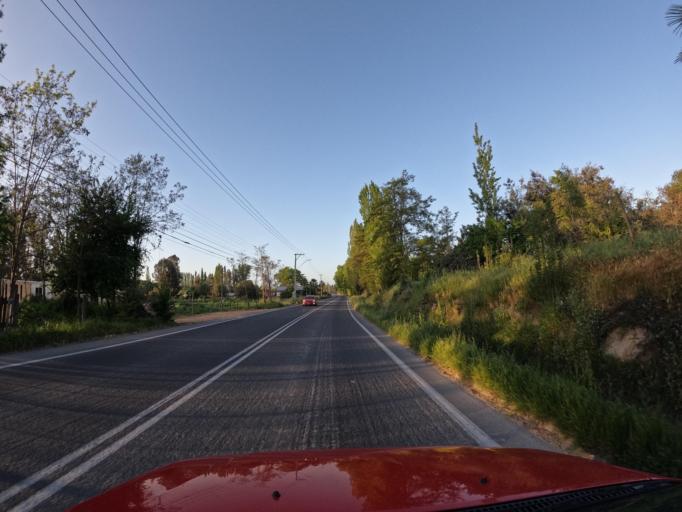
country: CL
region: O'Higgins
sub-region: Provincia de Cachapoal
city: San Vicente
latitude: -34.1887
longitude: -71.4031
